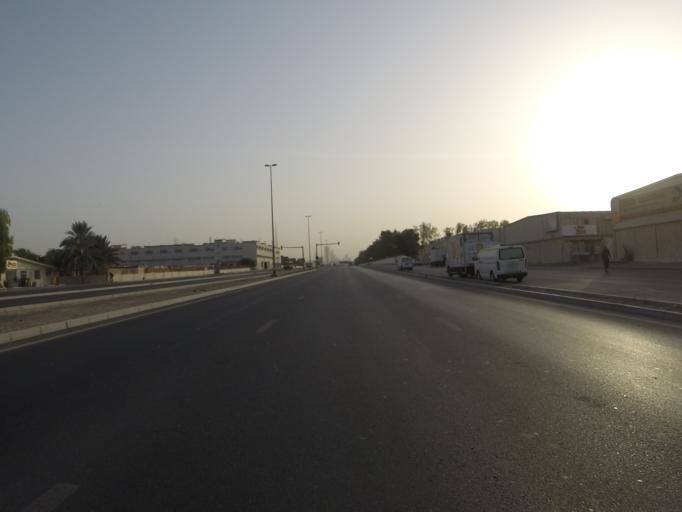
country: AE
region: Dubai
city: Dubai
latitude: 25.1415
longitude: 55.2419
